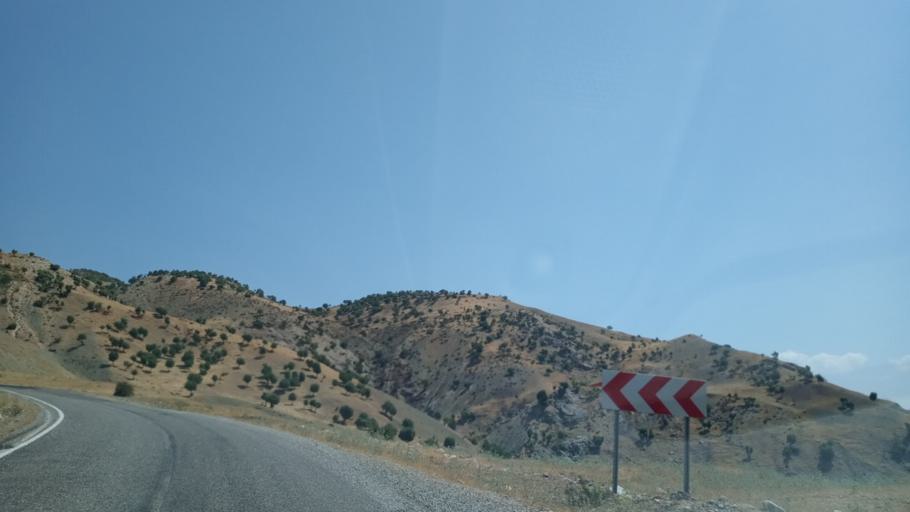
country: TR
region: Siirt
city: Dilektepe
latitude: 38.0645
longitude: 41.8323
